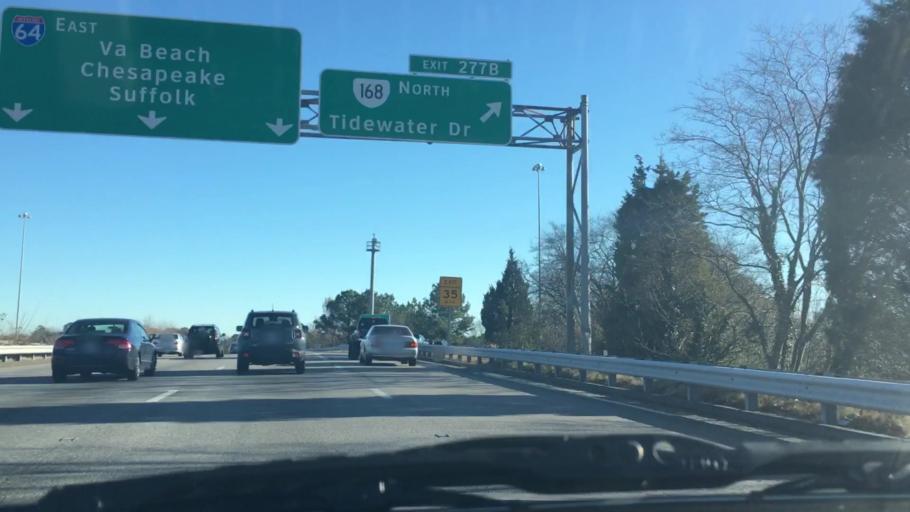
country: US
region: Virginia
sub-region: City of Norfolk
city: Norfolk
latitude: 36.9057
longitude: -76.2557
